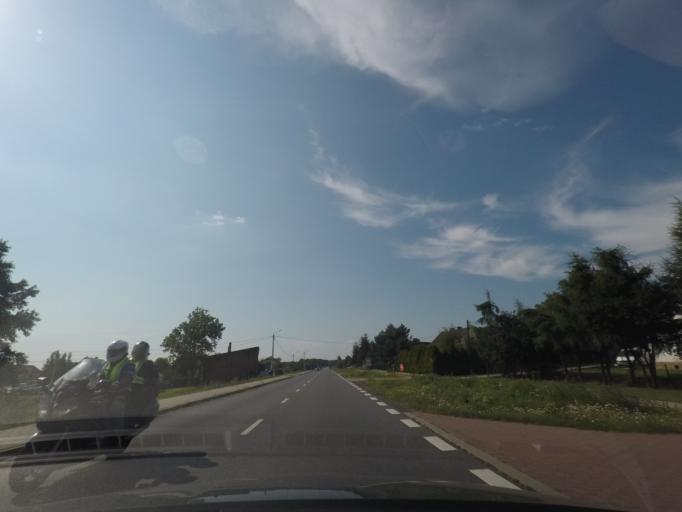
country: PL
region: Silesian Voivodeship
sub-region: Powiat pszczynski
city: Radostowice
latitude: 50.0099
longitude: 18.8633
